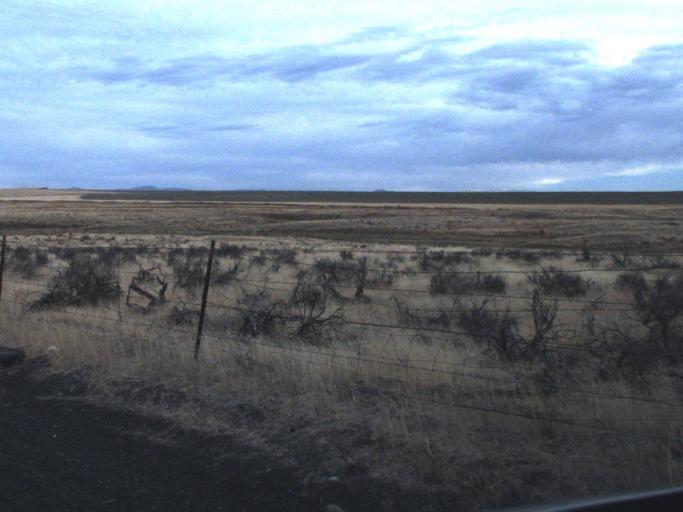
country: US
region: Washington
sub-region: Okanogan County
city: Coulee Dam
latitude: 47.6866
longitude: -118.7219
